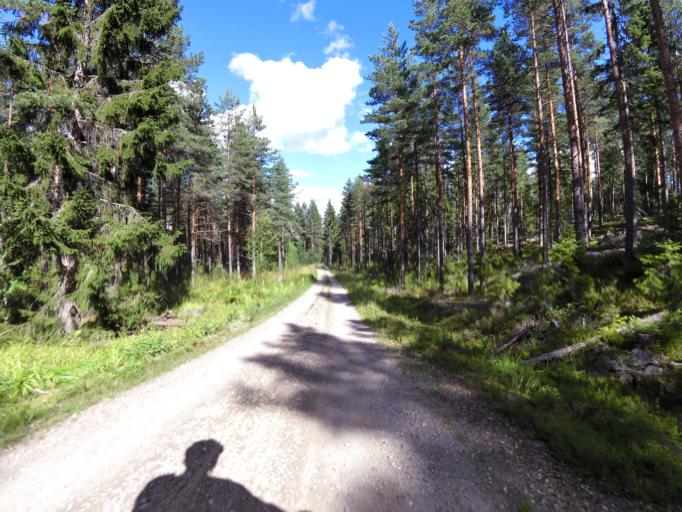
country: SE
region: Gaevleborg
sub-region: Ockelbo Kommun
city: Ockelbo
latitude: 60.8360
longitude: 16.7928
